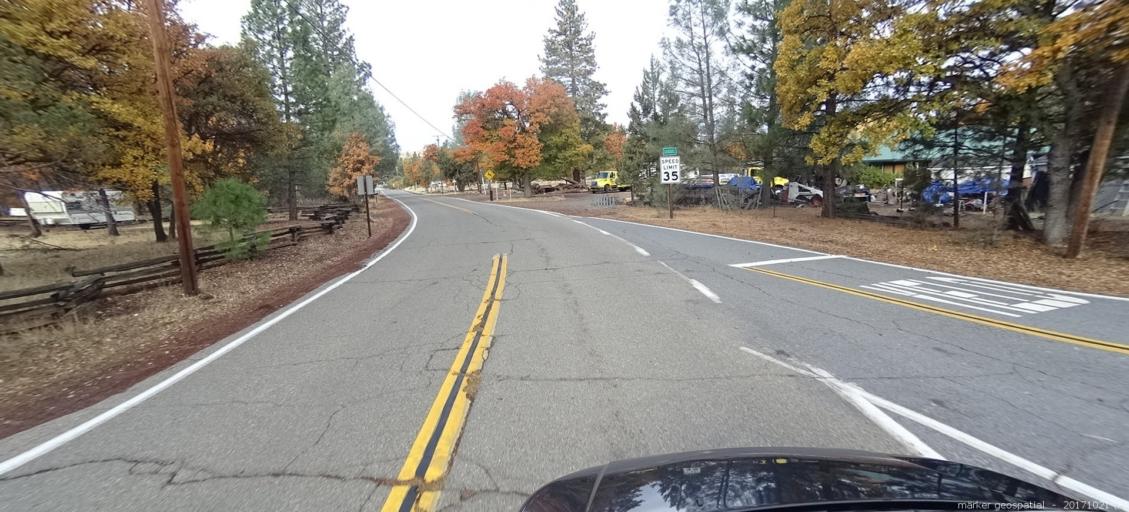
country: US
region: California
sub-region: Shasta County
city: Burney
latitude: 40.9185
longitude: -121.5475
